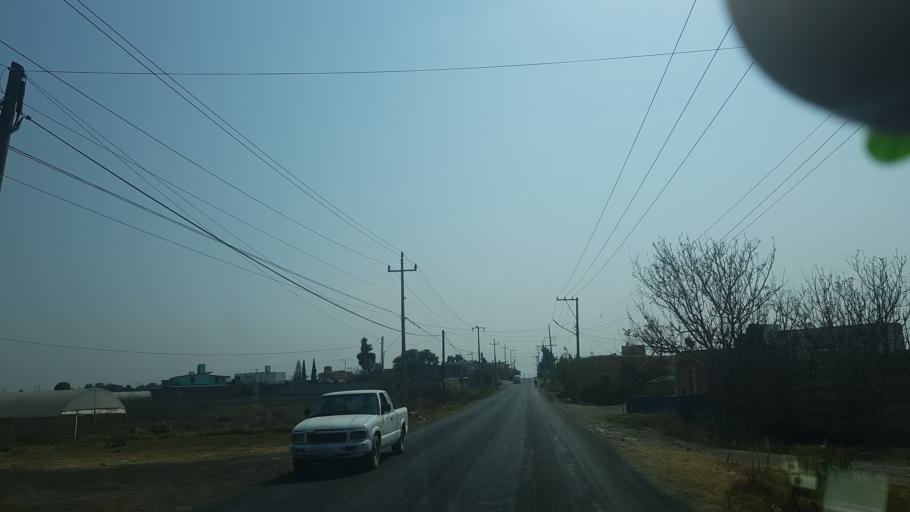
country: MX
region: Puebla
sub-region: San Jeronimo Tecuanipan
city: Los Reyes Tlanechicolpan
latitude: 19.0537
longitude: -98.3392
